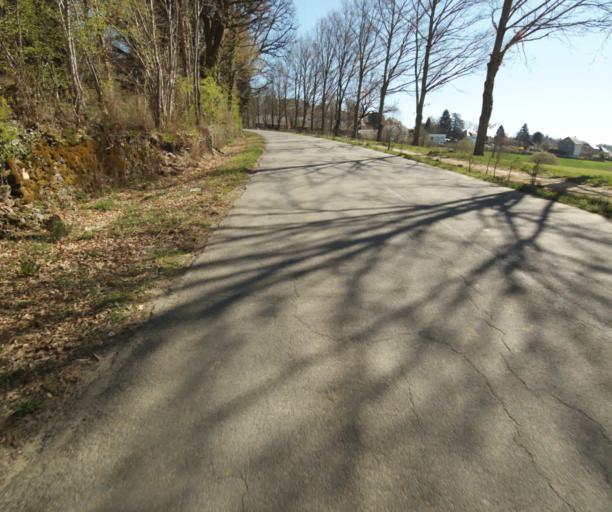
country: FR
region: Limousin
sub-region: Departement de la Correze
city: Seilhac
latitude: 45.3654
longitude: 1.7103
